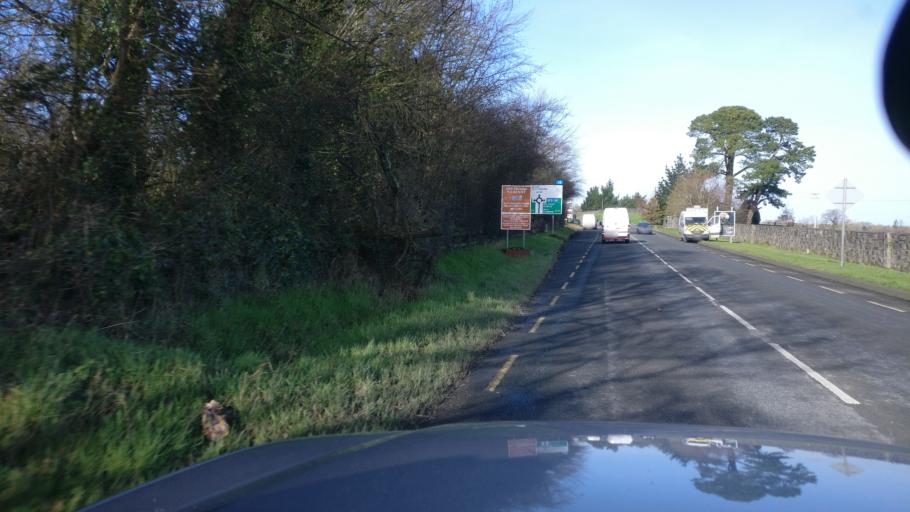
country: IE
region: Leinster
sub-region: Kilkenny
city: Kilkenny
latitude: 52.6390
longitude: -7.2283
